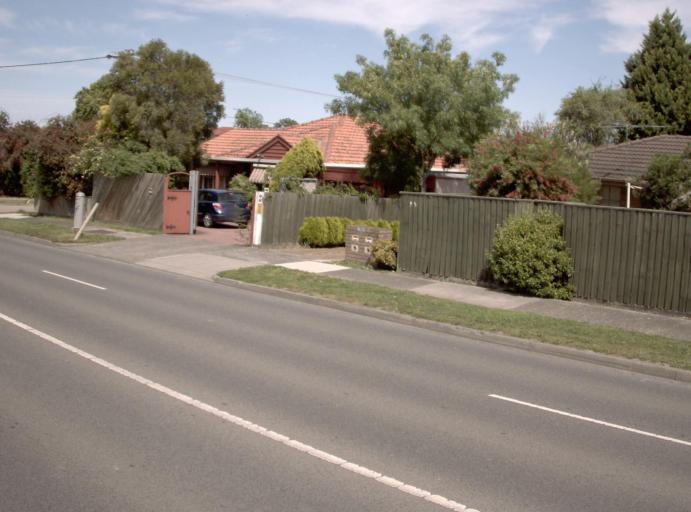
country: AU
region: Victoria
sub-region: Manningham
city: Doncaster East
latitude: -37.7932
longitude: 145.1613
